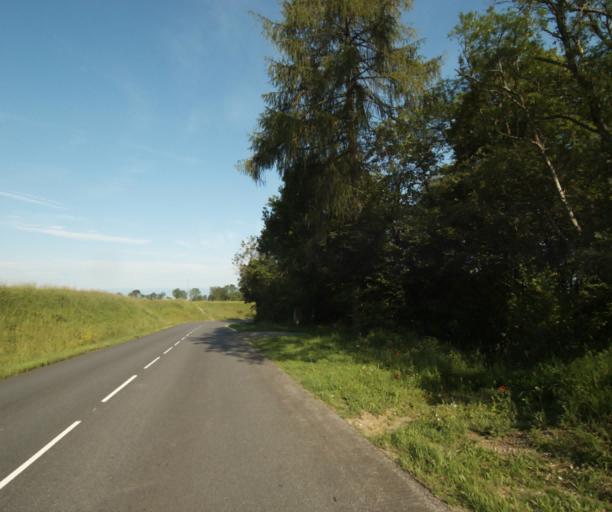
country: FR
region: Rhone-Alpes
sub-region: Departement de la Haute-Savoie
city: Lyaud
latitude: 46.3430
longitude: 6.5311
